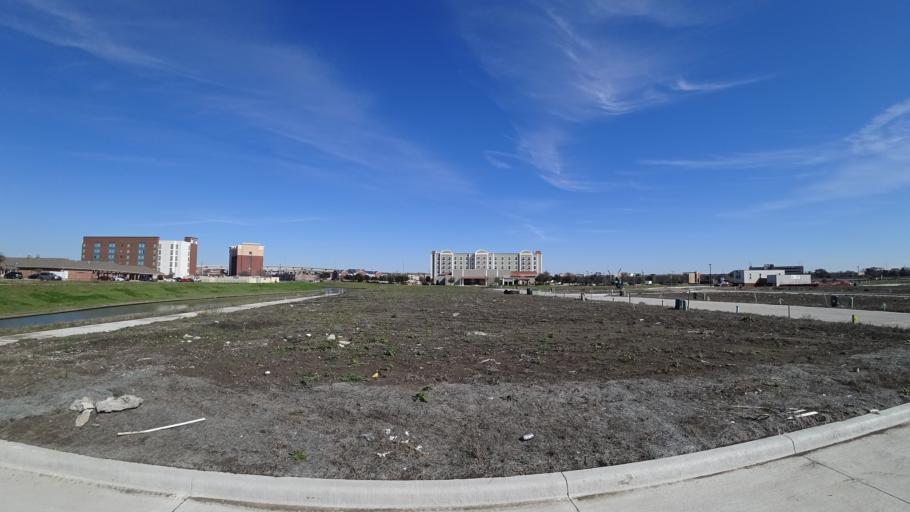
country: US
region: Texas
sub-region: Denton County
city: Lewisville
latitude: 32.9968
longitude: -96.9705
